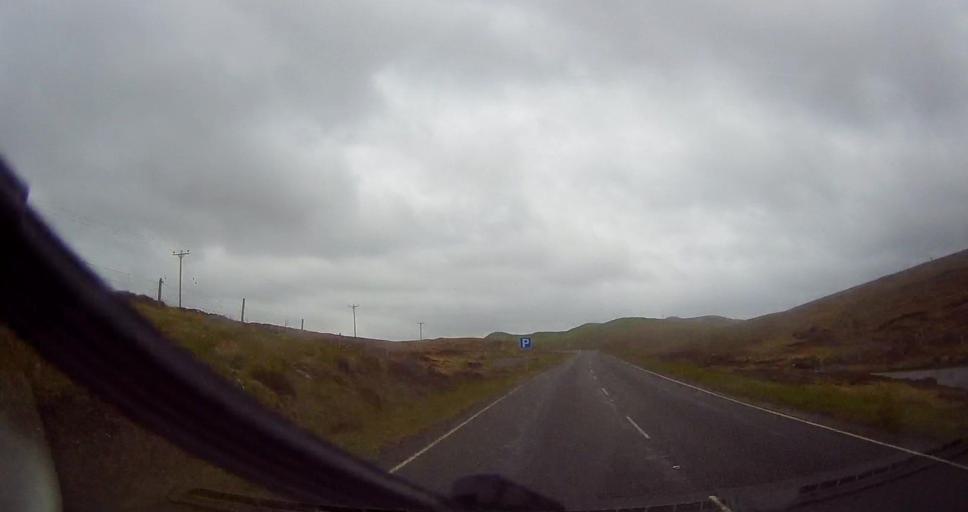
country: GB
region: Scotland
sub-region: Shetland Islands
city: Lerwick
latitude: 60.4366
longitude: -1.3972
